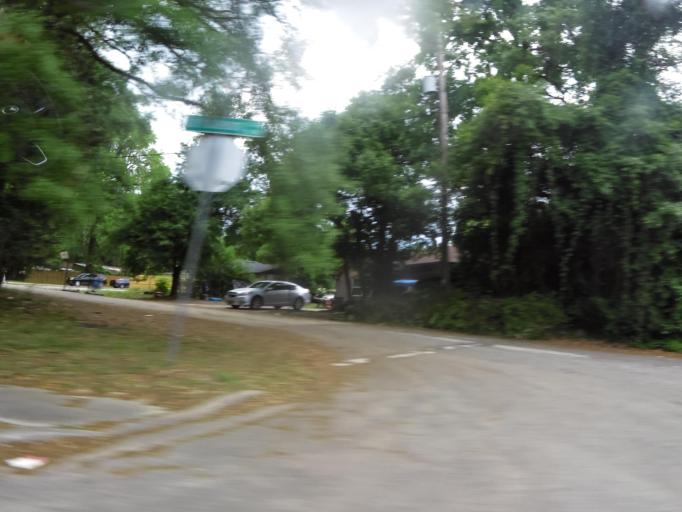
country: US
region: Florida
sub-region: Duval County
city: Jacksonville
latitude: 30.2971
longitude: -81.7592
